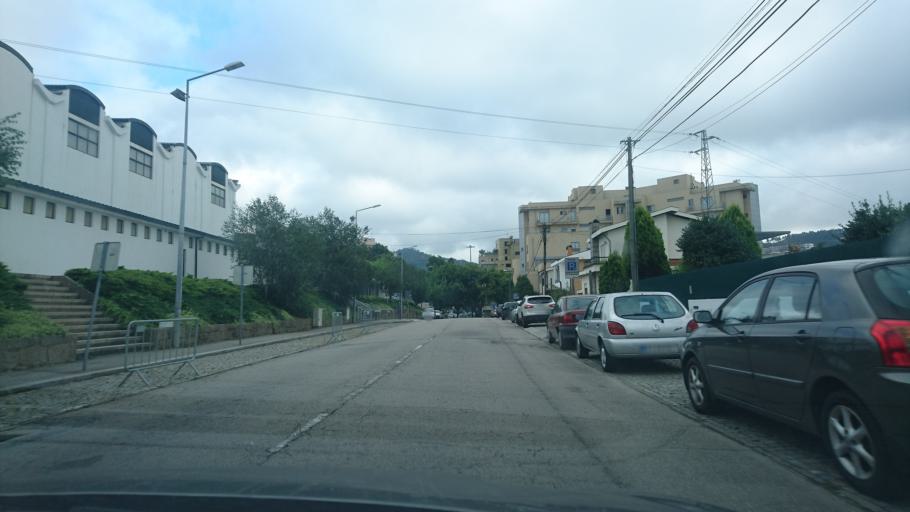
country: PT
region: Porto
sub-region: Valongo
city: Valongo
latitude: 41.1951
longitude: -8.5014
